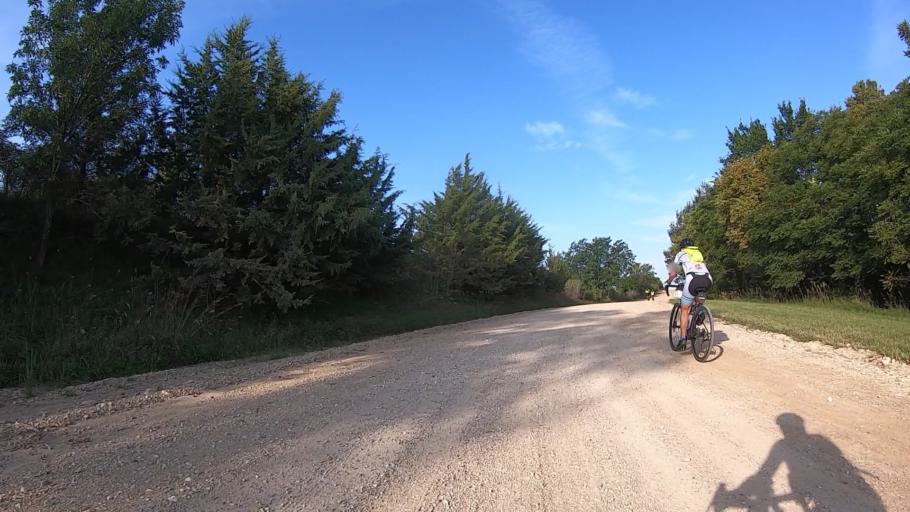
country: US
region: Kansas
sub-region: Marshall County
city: Blue Rapids
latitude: 39.6753
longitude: -96.7842
